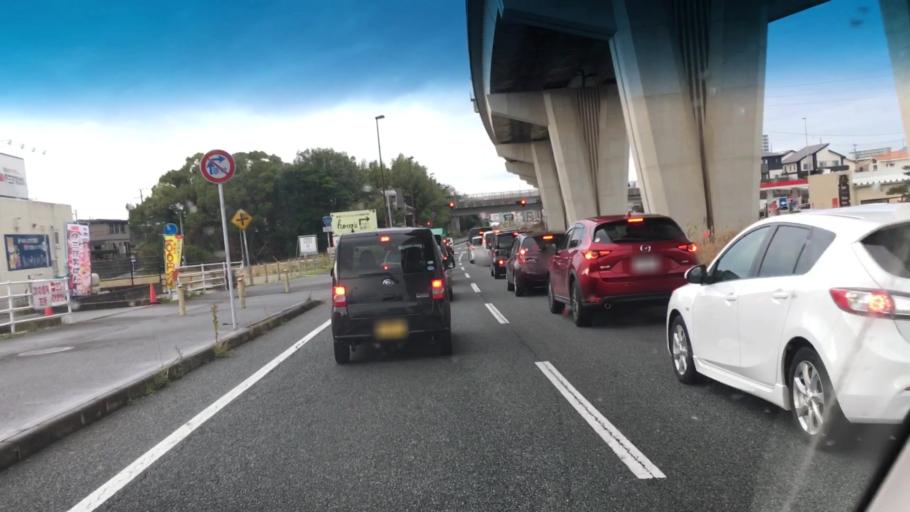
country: JP
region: Fukuoka
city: Maebaru-chuo
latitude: 33.5728
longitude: 130.2685
